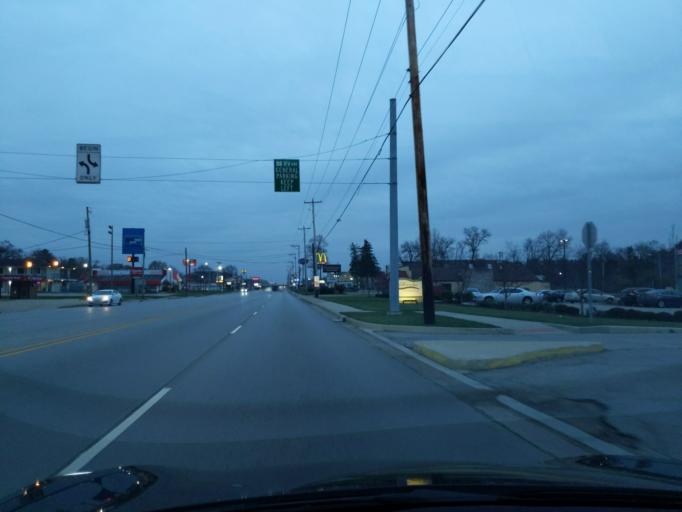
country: US
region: Indiana
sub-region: Saint Joseph County
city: Georgetown
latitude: 41.7297
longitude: -86.2508
